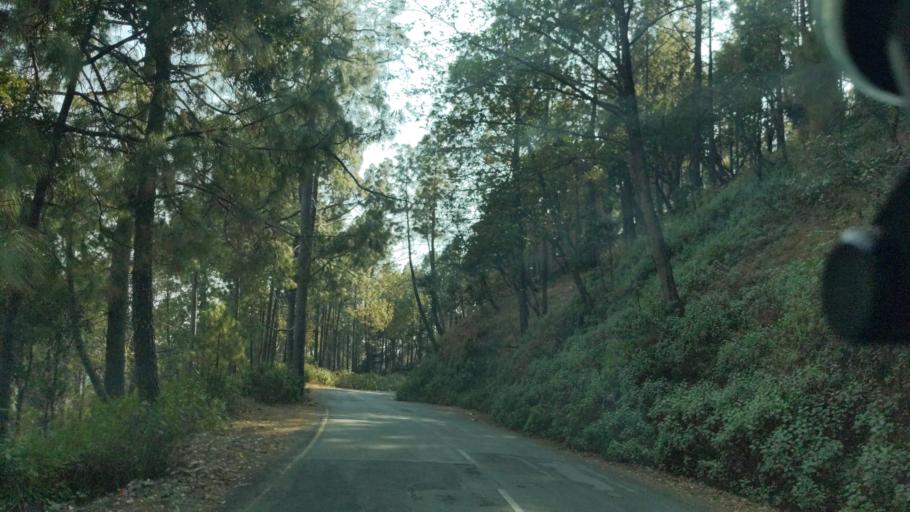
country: IN
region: Uttarakhand
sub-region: Naini Tal
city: Bhowali
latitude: 29.4010
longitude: 79.5381
